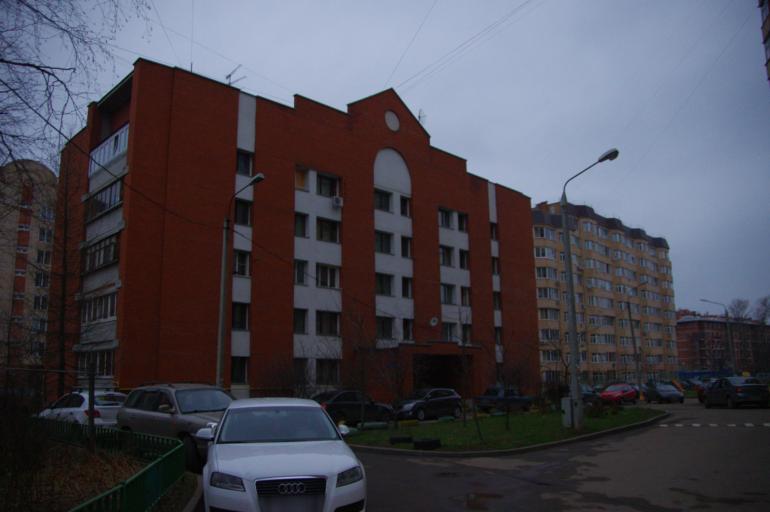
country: RU
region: Moskovskaya
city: Opalikha
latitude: 55.8313
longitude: 37.2405
